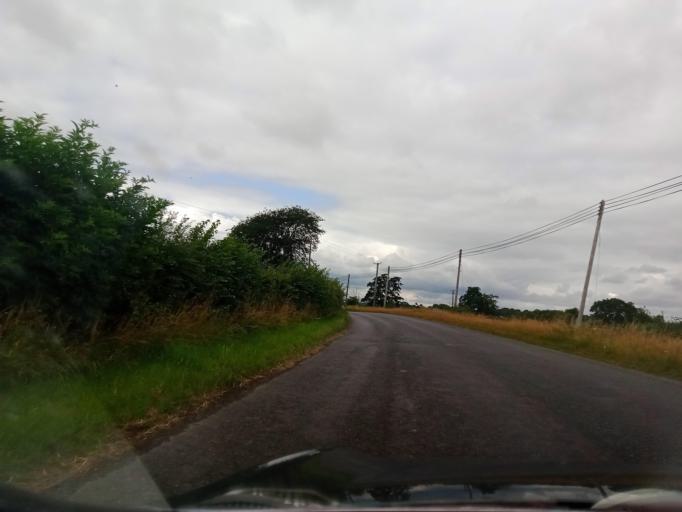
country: IE
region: Leinster
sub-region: Laois
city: Stradbally
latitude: 52.9811
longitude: -7.1805
